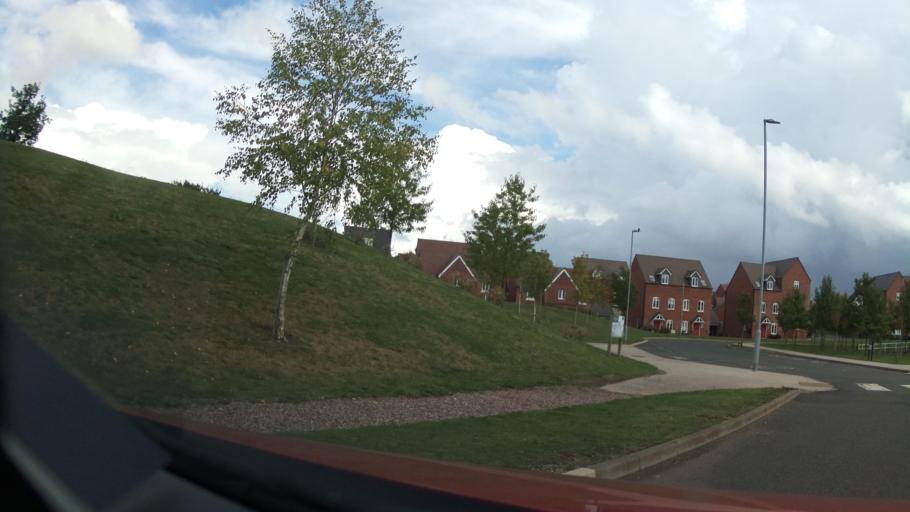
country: GB
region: England
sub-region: Staffordshire
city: Barlaston
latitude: 52.9561
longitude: -2.1698
